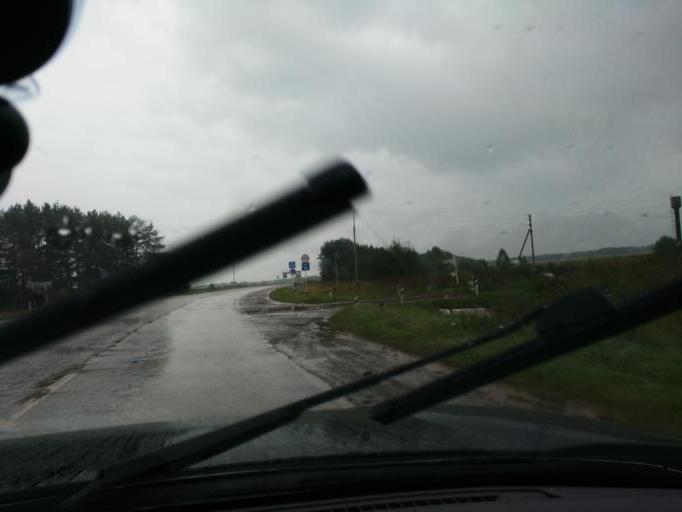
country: RU
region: Perm
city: Osa
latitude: 57.2903
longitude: 55.5790
